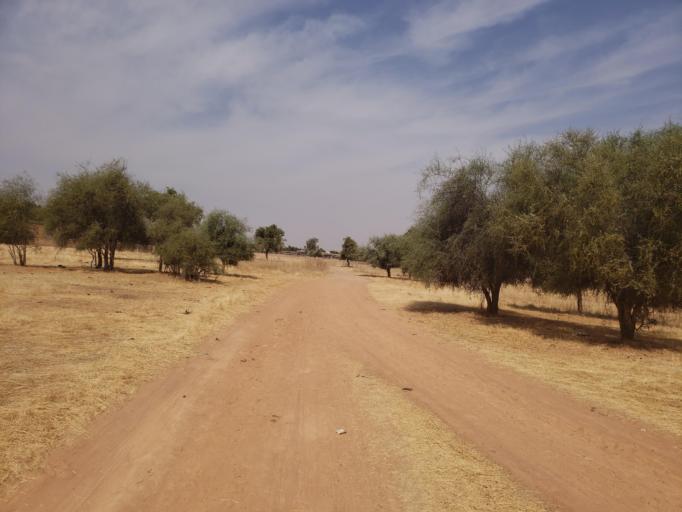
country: SN
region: Matam
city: Ranerou
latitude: 15.2931
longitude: -13.9628
